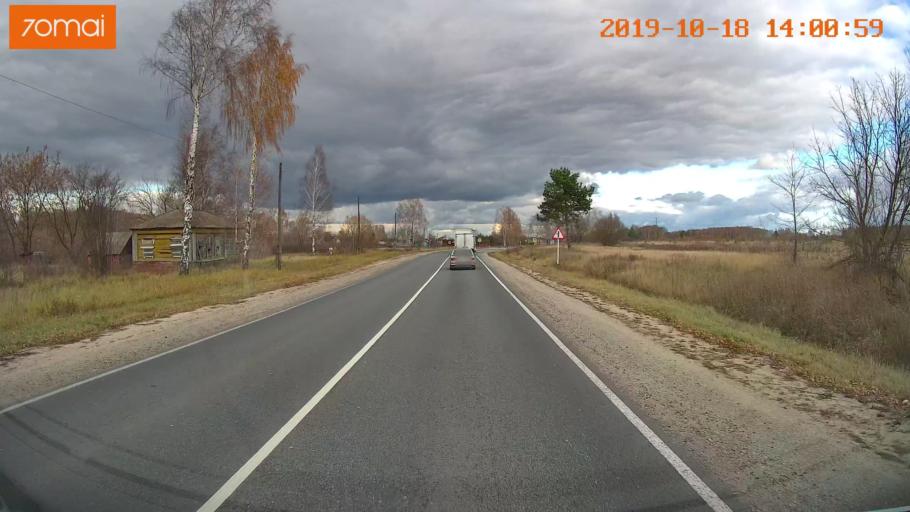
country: RU
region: Rjazan
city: Spas-Klepiki
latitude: 55.1047
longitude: 40.0827
